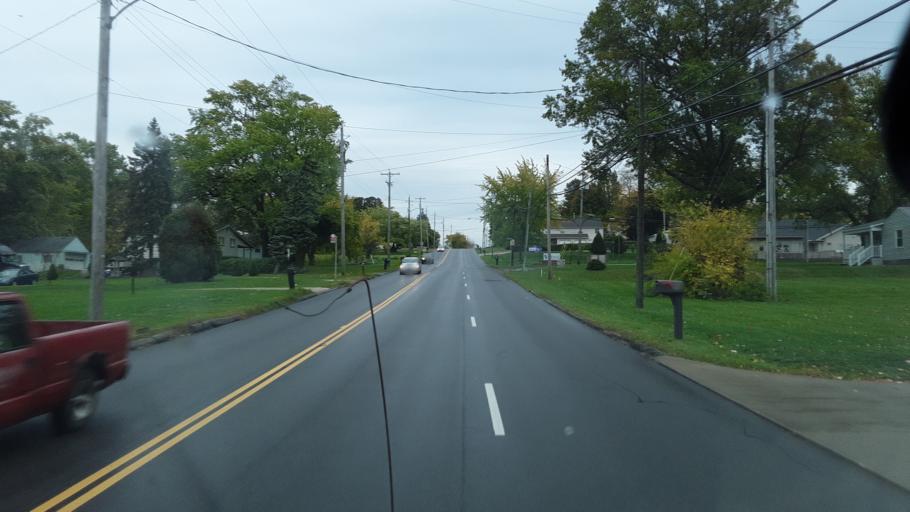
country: US
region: Ohio
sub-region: Summit County
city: Portage Lakes
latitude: 41.0295
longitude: -81.5000
